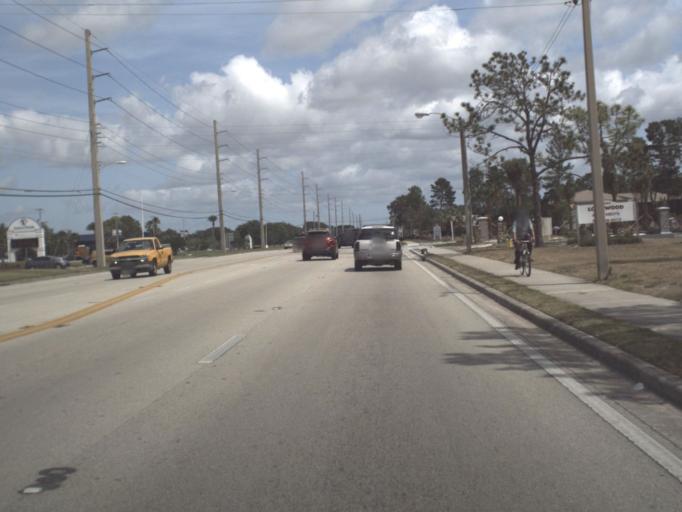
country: US
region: Florida
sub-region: Brevard County
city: Cocoa
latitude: 28.3837
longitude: -80.7550
